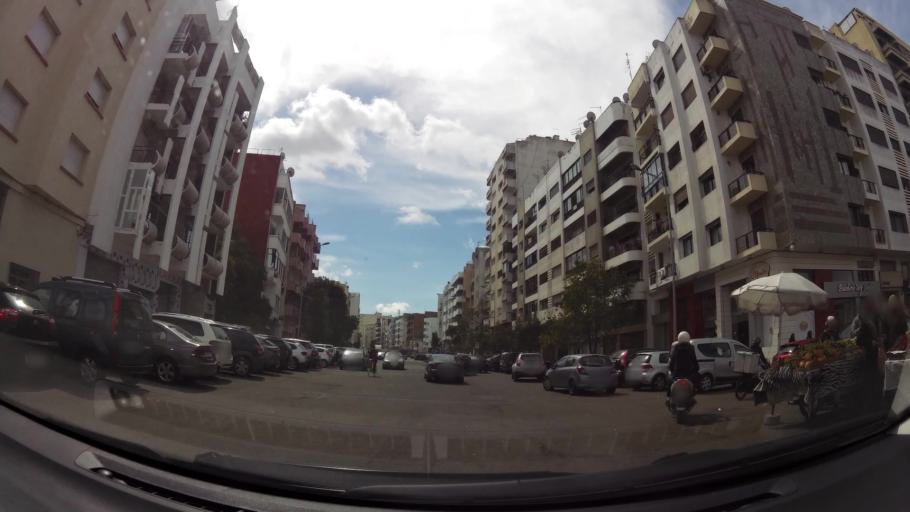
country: MA
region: Grand Casablanca
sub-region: Casablanca
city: Casablanca
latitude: 33.5836
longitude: -7.6441
